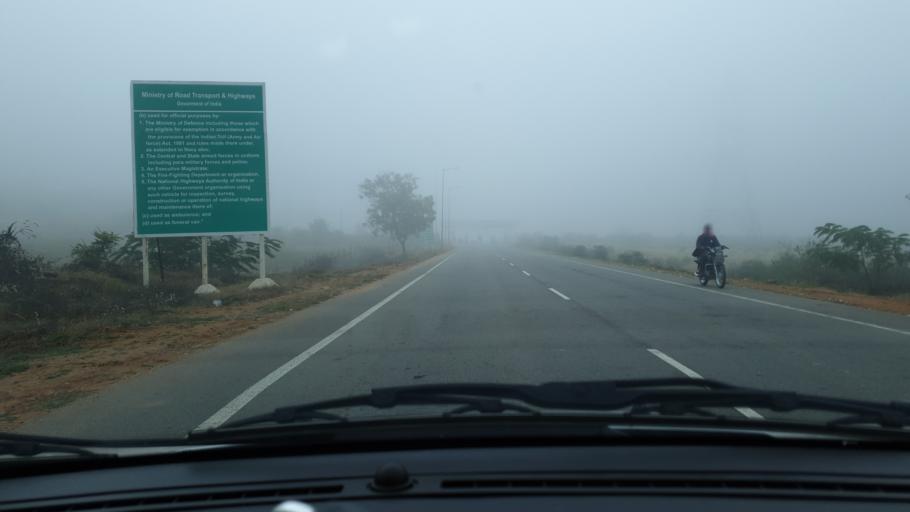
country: IN
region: Telangana
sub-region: Nalgonda
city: Devarkonda
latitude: 16.6144
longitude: 78.6749
